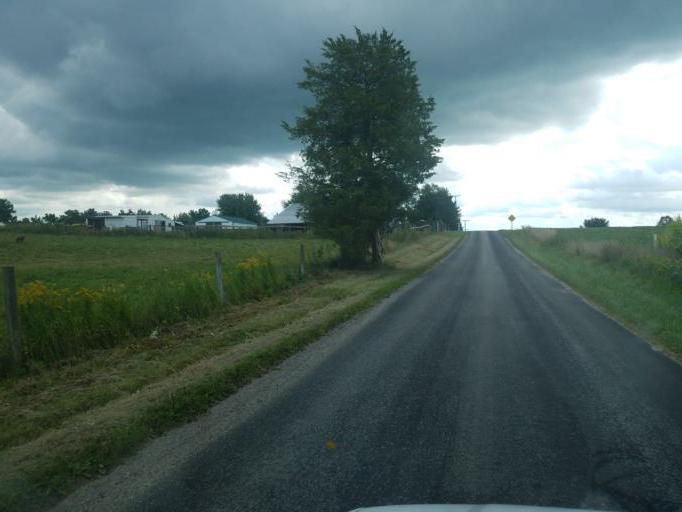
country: US
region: Ohio
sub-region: Huron County
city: Greenwich
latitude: 40.9776
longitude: -82.5346
